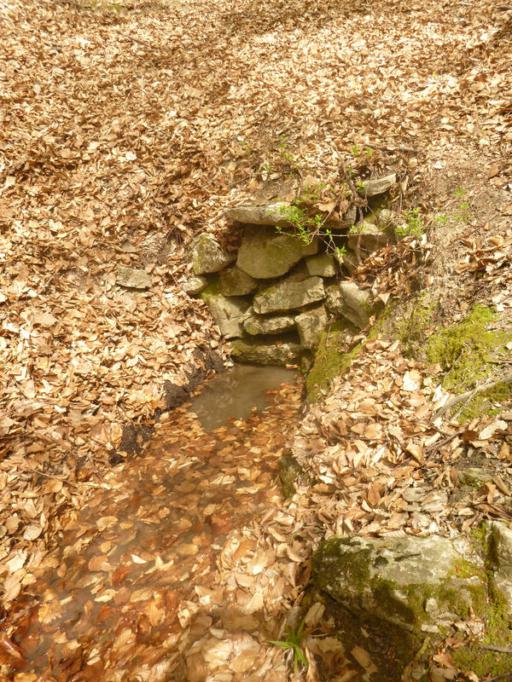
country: HU
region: Baranya
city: Hosszuheteny
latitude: 46.2183
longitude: 18.3593
